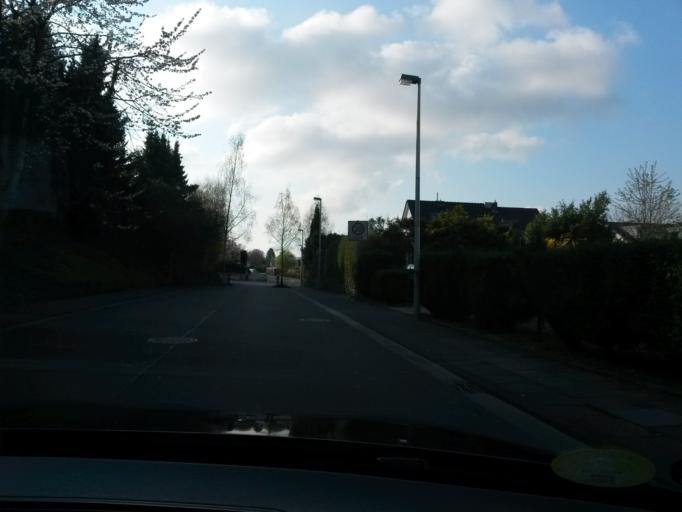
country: DE
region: North Rhine-Westphalia
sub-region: Regierungsbezirk Koln
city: Alfter
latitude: 50.7108
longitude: 7.0410
